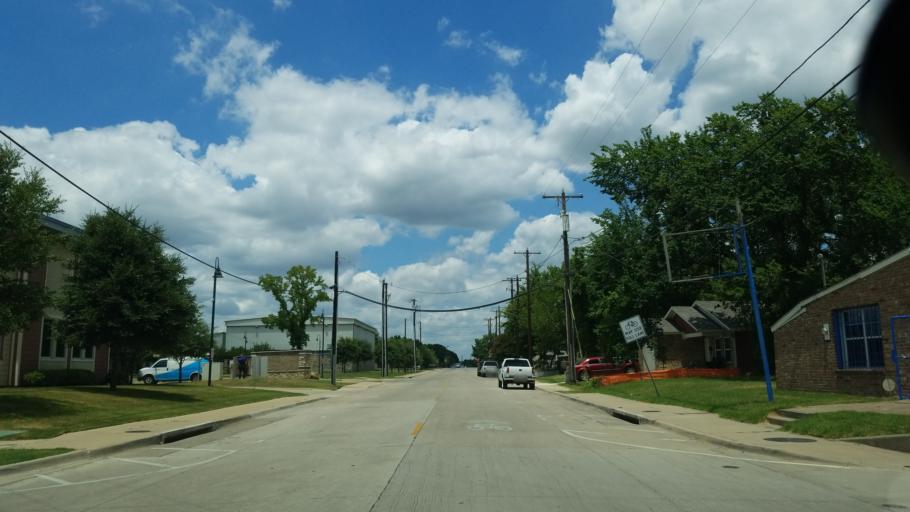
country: US
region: Texas
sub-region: Dallas County
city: Dallas
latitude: 32.7362
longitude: -96.7535
